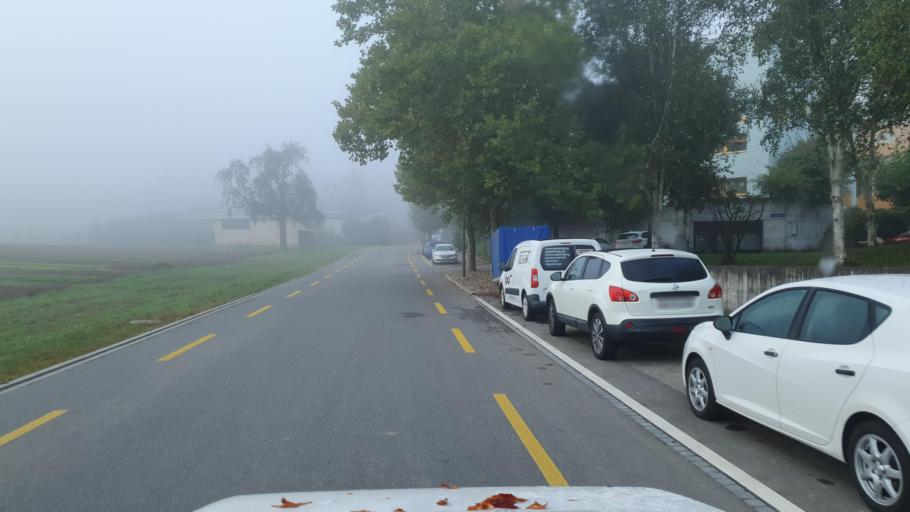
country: CH
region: Aargau
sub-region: Bezirk Baden
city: Baden
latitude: 47.4501
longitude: 8.2863
